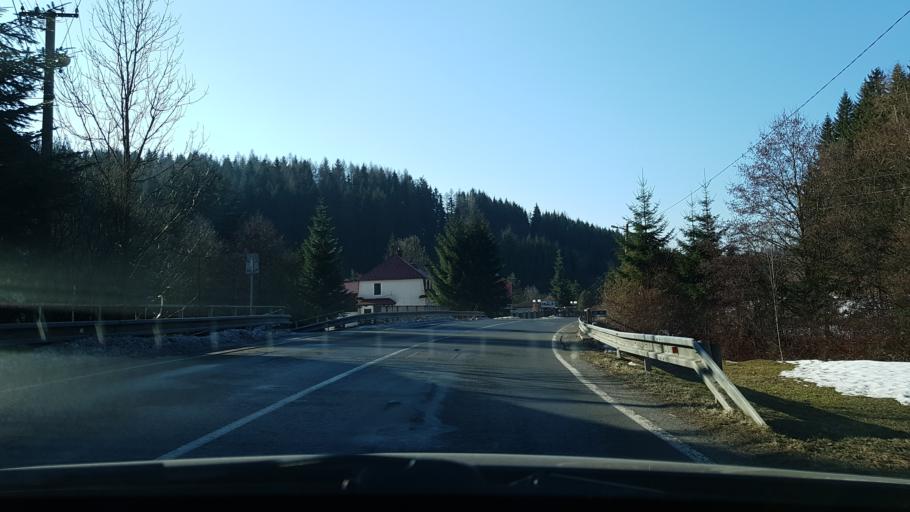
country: CZ
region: Olomoucky
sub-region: Okres Sumperk
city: Stare Mesto
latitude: 50.1132
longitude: 17.0052
